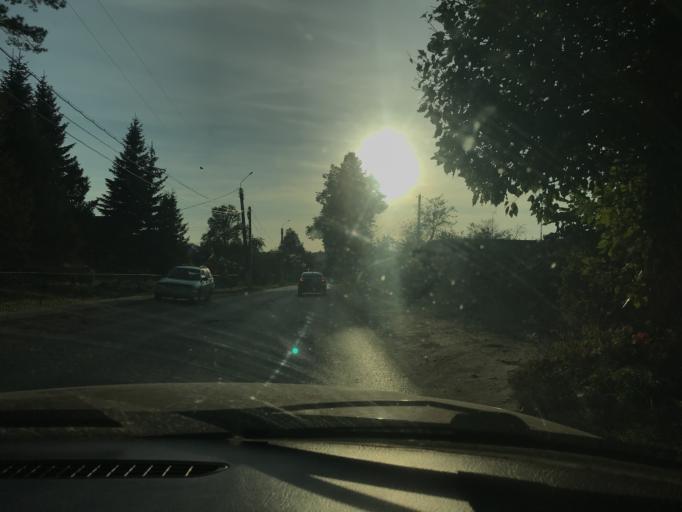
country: RU
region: Kaluga
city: Kondrovo
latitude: 54.7821
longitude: 35.9383
